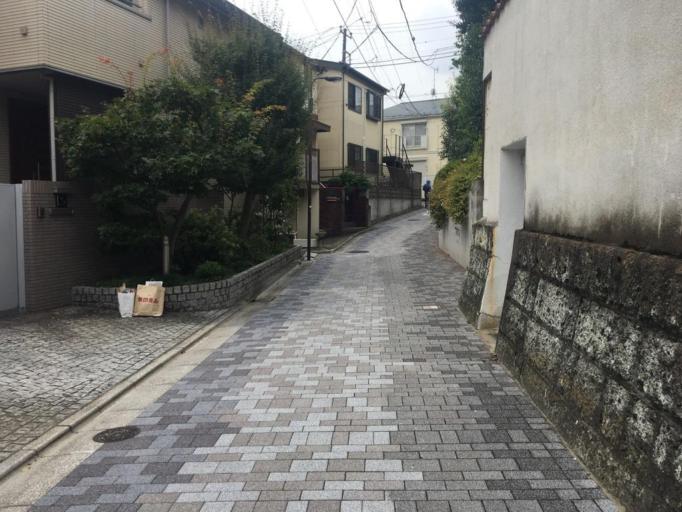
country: JP
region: Tokyo
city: Tokyo
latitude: 35.7206
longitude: 139.7002
